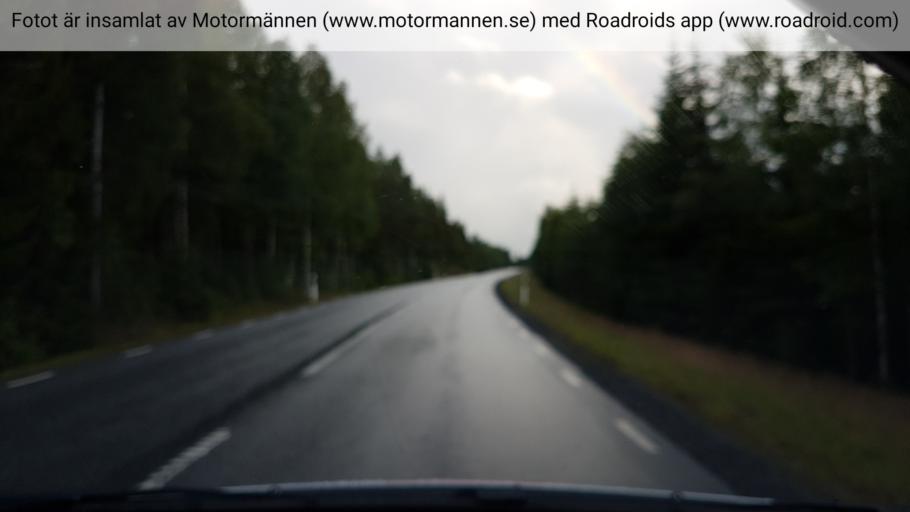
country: SE
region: OErebro
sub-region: Nora Kommun
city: As
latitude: 59.5302
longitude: 14.8191
